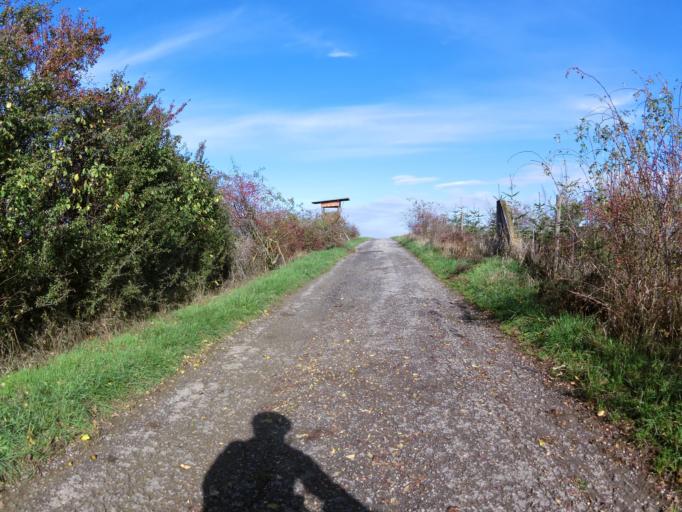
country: DE
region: Bavaria
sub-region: Regierungsbezirk Unterfranken
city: Sommerhausen
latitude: 49.7137
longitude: 10.0390
